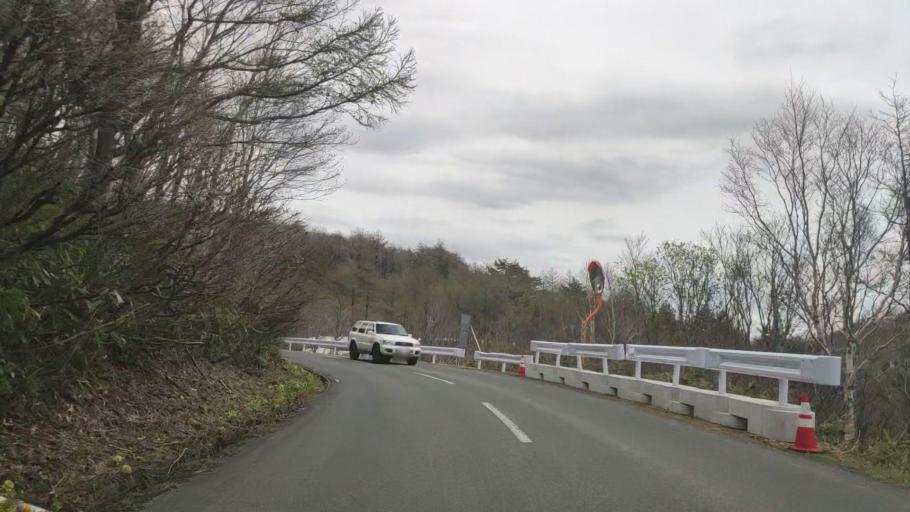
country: JP
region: Aomori
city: Aomori Shi
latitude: 40.7147
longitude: 140.8698
